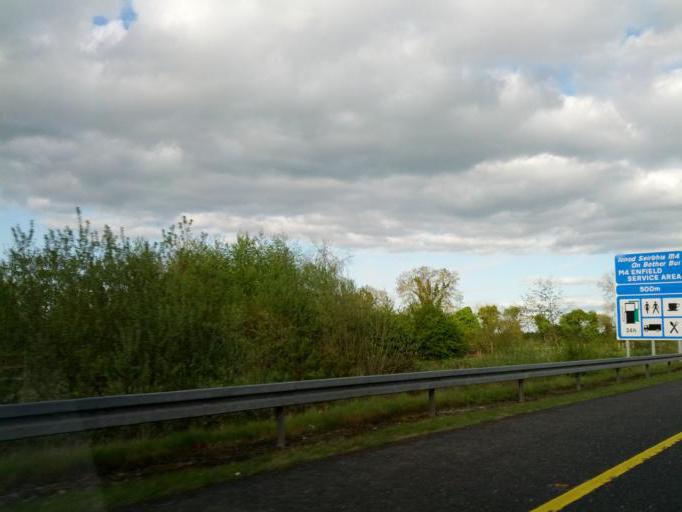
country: IE
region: Leinster
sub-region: An Mhi
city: Longwood
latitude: 53.4119
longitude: -6.8943
